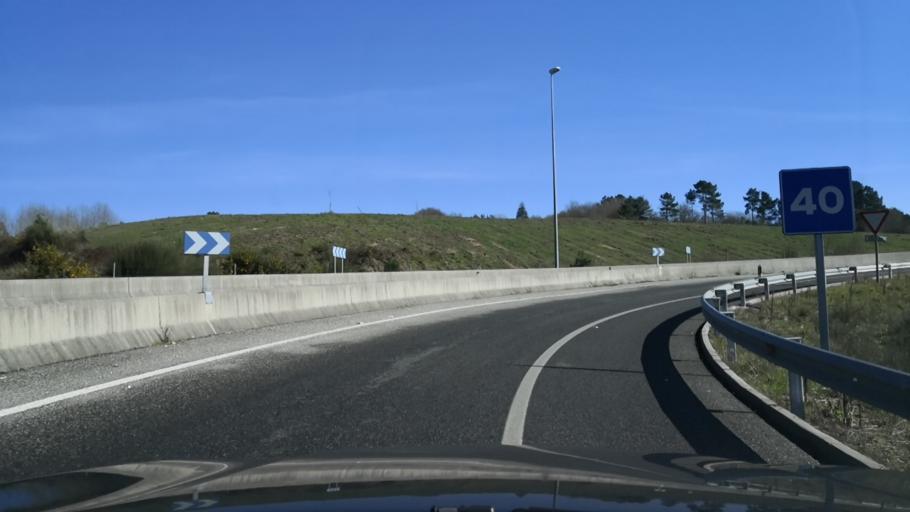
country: ES
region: Galicia
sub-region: Provincia de Ourense
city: Maside
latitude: 42.4495
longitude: -8.0222
